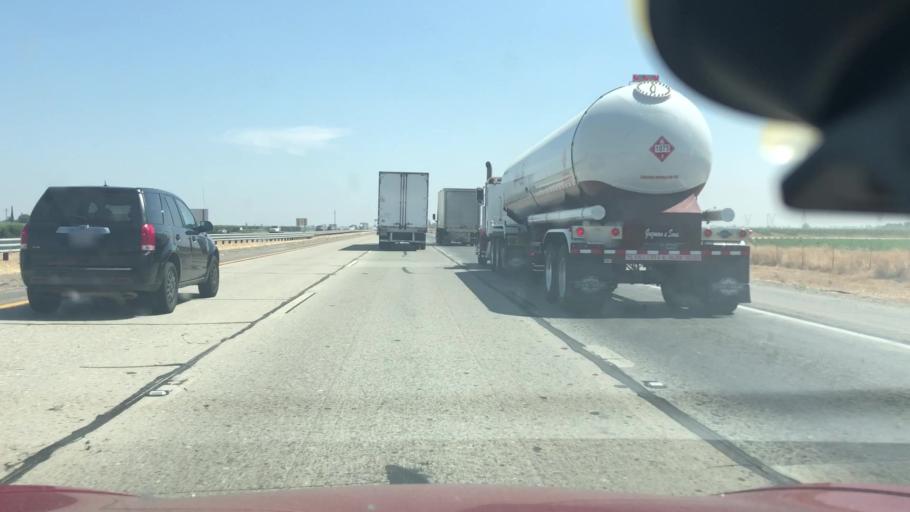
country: US
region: California
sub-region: San Joaquin County
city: Woodbridge
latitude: 38.1058
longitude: -121.3913
